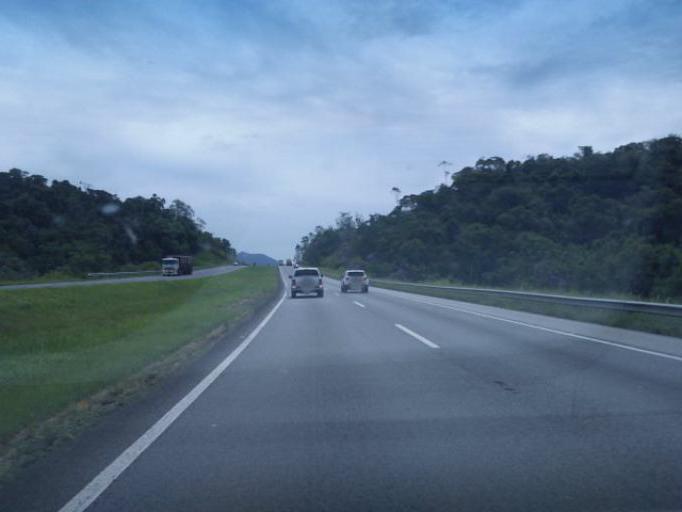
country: BR
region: Sao Paulo
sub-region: Juquia
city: Juquia
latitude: -24.3300
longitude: -47.5815
